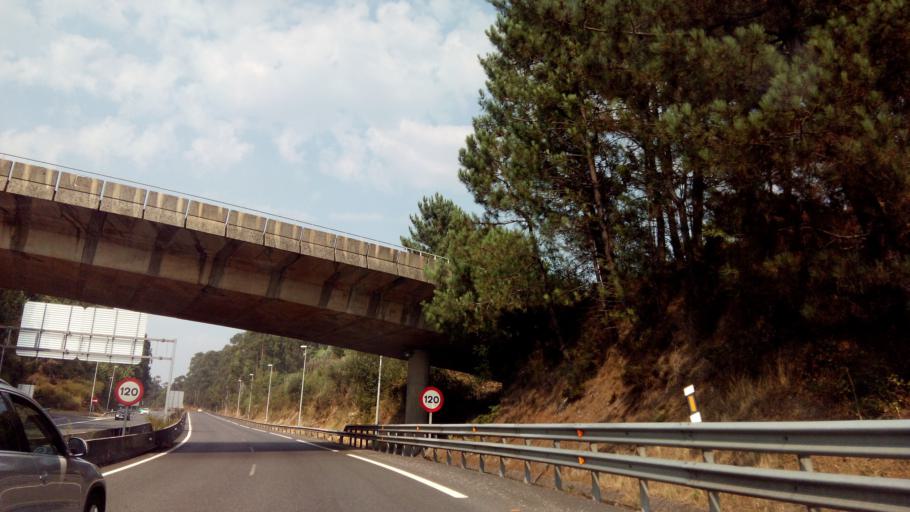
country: ES
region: Galicia
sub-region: Provincia de Pontevedra
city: Tui
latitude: 42.0679
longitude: -8.6349
